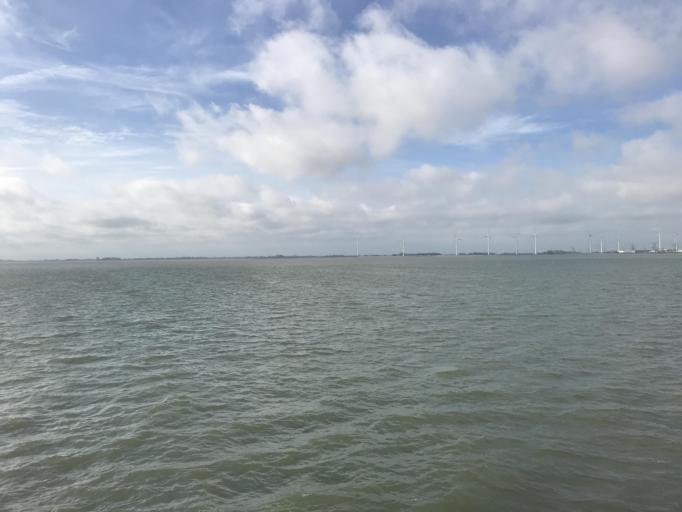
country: NL
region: Groningen
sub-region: Gemeente Delfzijl
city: Delfzijl
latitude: 53.4262
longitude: 6.9228
